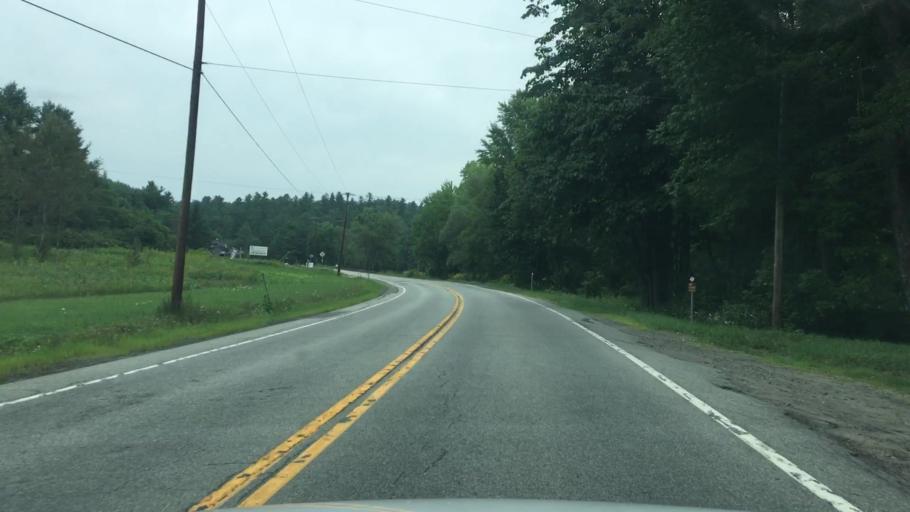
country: US
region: New York
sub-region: Essex County
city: Elizabethtown
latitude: 44.4137
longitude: -73.6810
